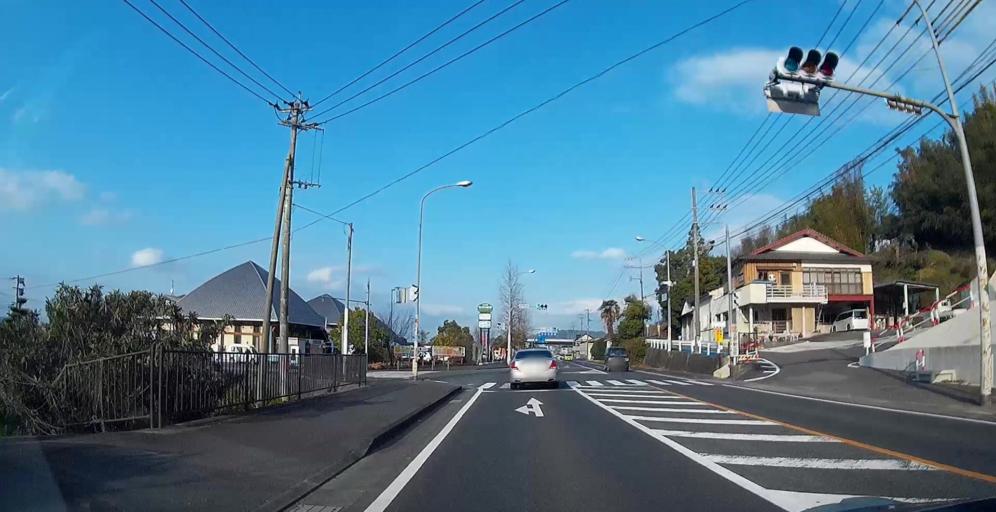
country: JP
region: Kumamoto
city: Matsubase
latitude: 32.5760
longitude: 130.6947
